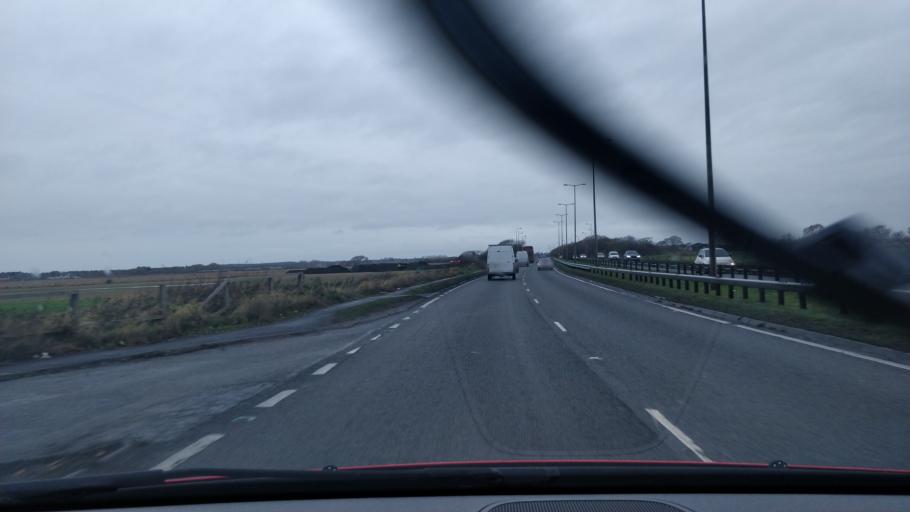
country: GB
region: England
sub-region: Sefton
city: Ince Blundell
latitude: 53.5320
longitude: -3.0387
